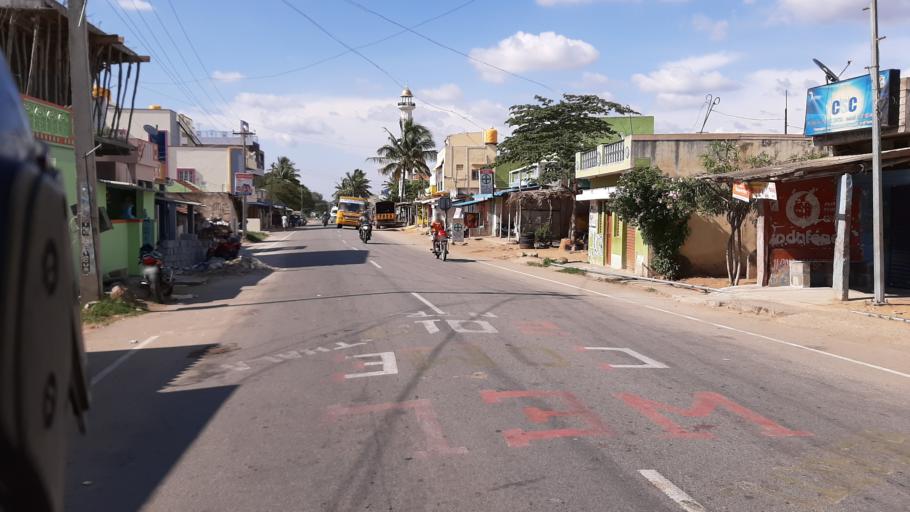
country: IN
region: Tamil Nadu
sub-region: Krishnagiri
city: Denkanikota
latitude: 12.5584
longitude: 77.7844
